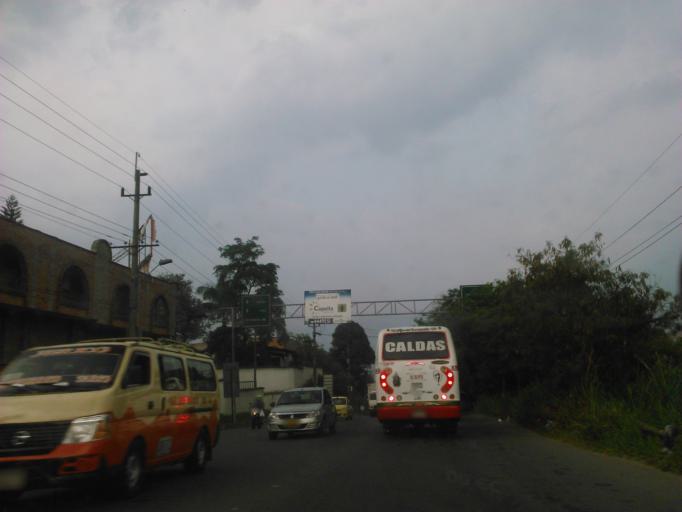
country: CO
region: Antioquia
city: La Estrella
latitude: 6.1525
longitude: -75.6330
